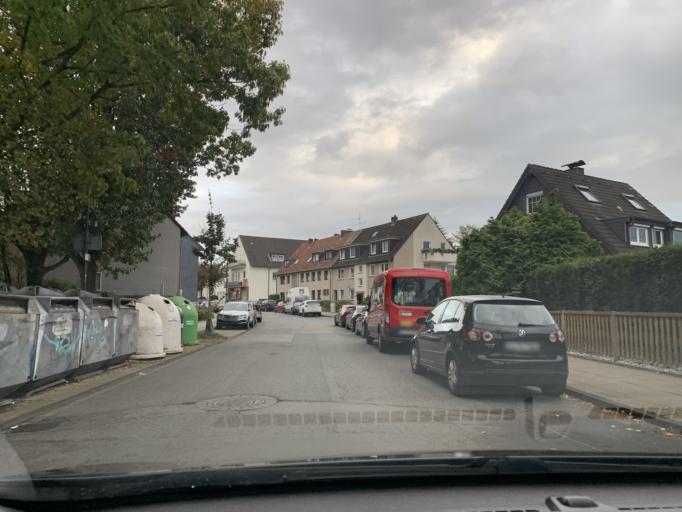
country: DE
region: North Rhine-Westphalia
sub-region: Regierungsbezirk Dusseldorf
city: Oberhausen
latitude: 51.4660
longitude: 6.9200
